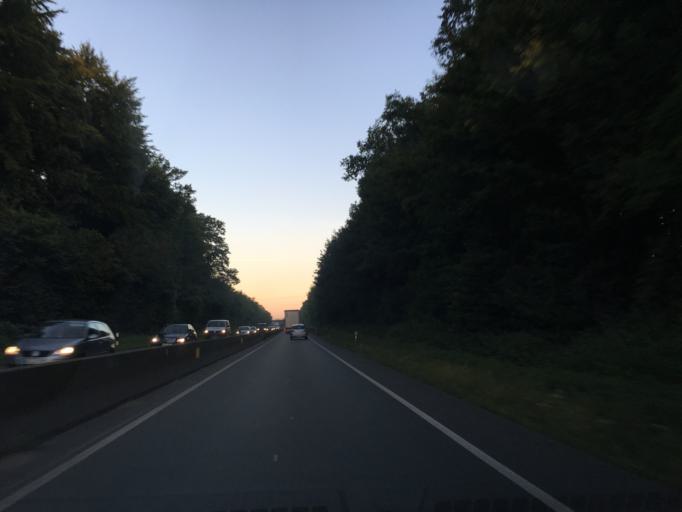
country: DE
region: North Rhine-Westphalia
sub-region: Regierungsbezirk Munster
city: Altenberge
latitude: 52.0173
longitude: 7.4979
